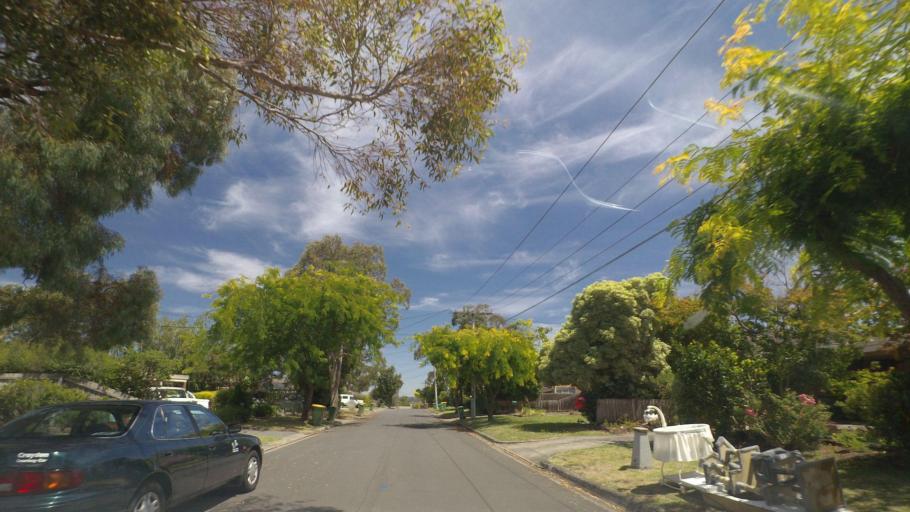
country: AU
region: Victoria
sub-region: Maroondah
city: Croydon North
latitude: -37.7690
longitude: 145.3172
